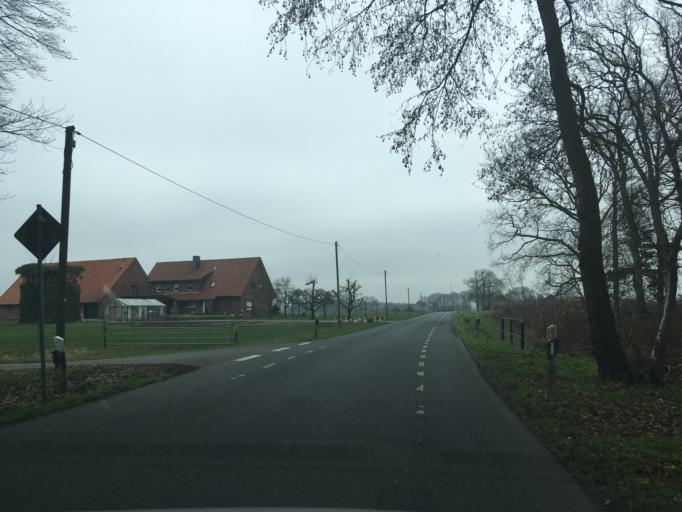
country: DE
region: North Rhine-Westphalia
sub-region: Regierungsbezirk Munster
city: Rhede
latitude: 51.8856
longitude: 6.7219
